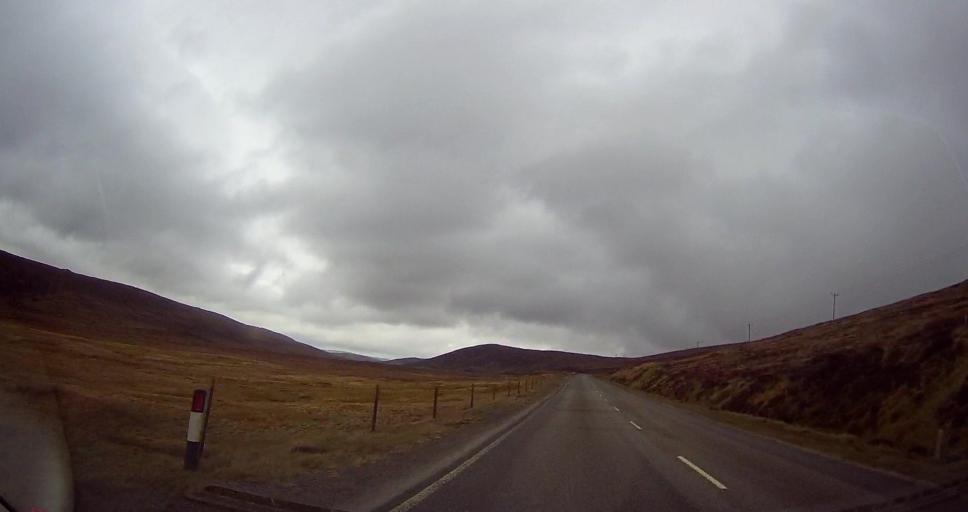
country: GB
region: Scotland
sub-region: Shetland Islands
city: Lerwick
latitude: 60.2889
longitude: -1.2410
